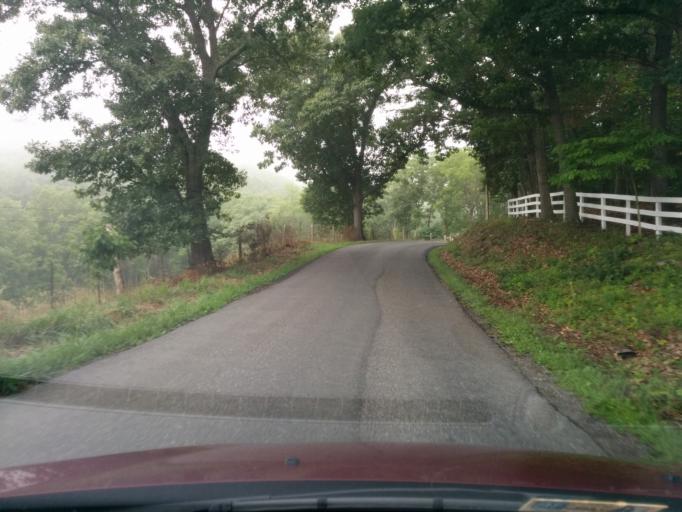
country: US
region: Virginia
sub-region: City of Lexington
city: Lexington
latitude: 37.7893
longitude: -79.4714
